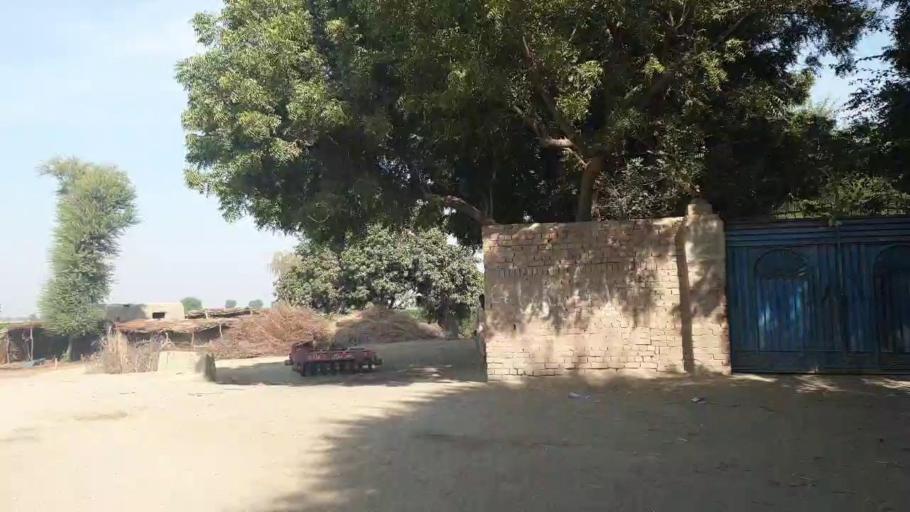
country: PK
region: Sindh
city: Matiari
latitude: 25.6788
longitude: 68.3484
